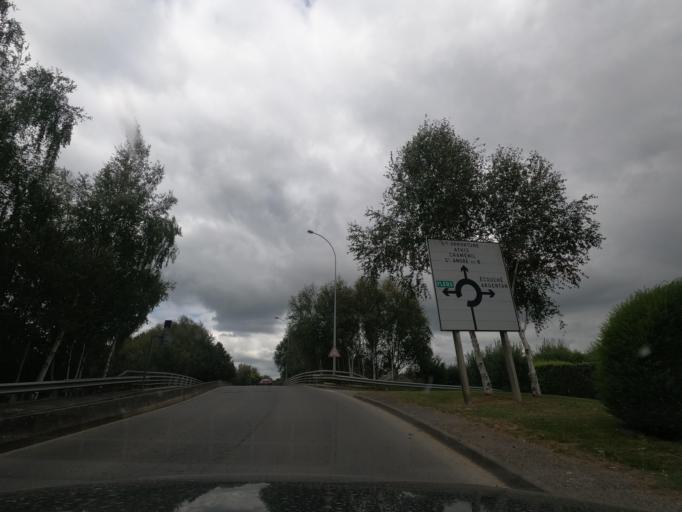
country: FR
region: Lower Normandy
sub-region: Departement de l'Orne
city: Briouze
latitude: 48.7017
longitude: -0.3659
